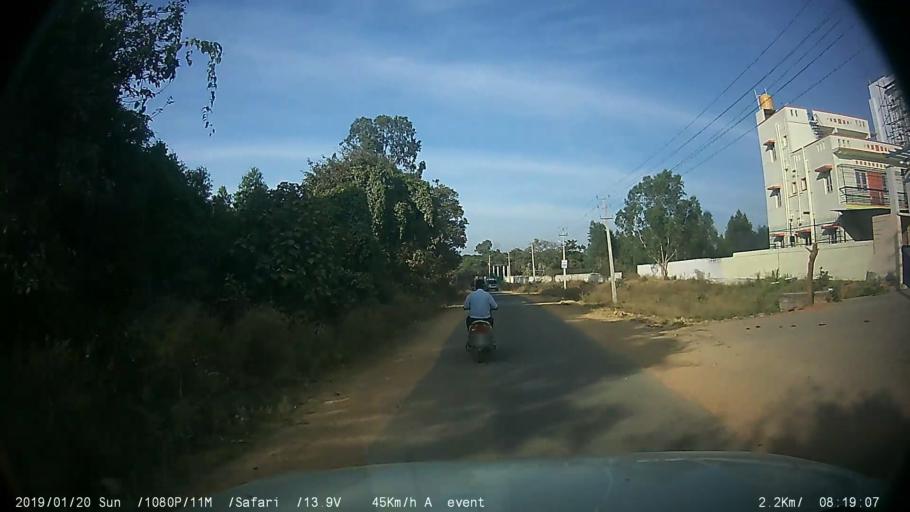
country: IN
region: Karnataka
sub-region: Bangalore Urban
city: Anekal
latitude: 12.8195
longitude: 77.6436
